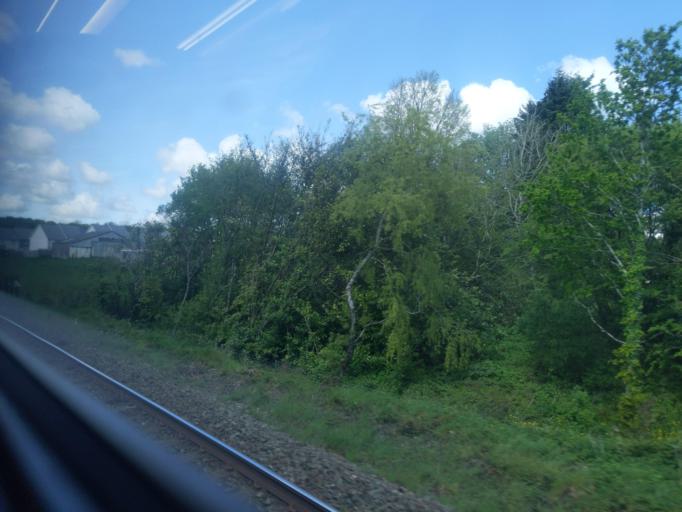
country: GB
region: England
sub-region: Cornwall
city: Liskeard
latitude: 50.4547
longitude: -4.5225
